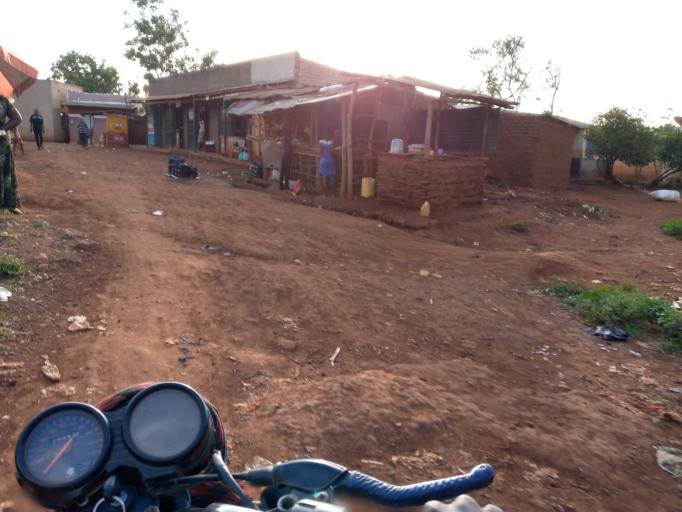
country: UG
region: Eastern Region
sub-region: Mbale District
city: Mbale
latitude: 1.0833
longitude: 34.1577
